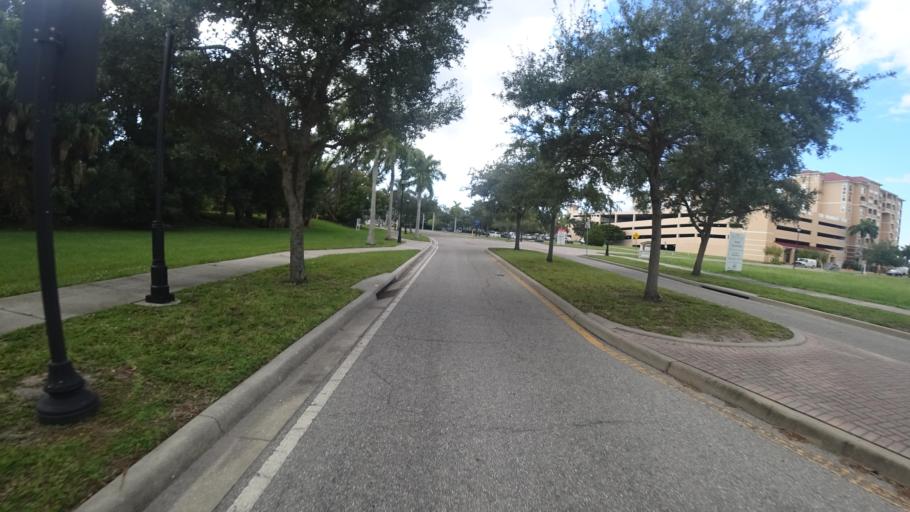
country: US
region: Florida
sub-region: Manatee County
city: Bradenton
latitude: 27.4974
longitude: -82.5692
